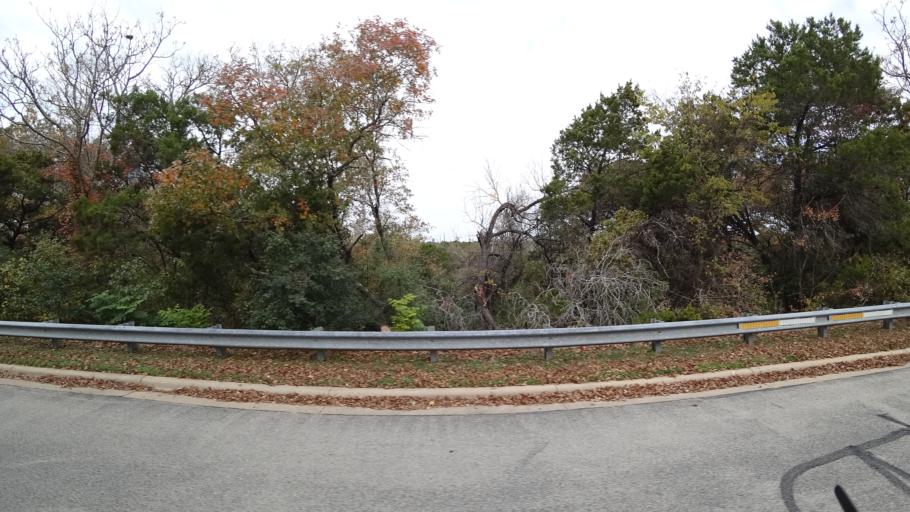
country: US
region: Texas
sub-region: Williamson County
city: Anderson Mill
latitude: 30.3938
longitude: -97.8372
